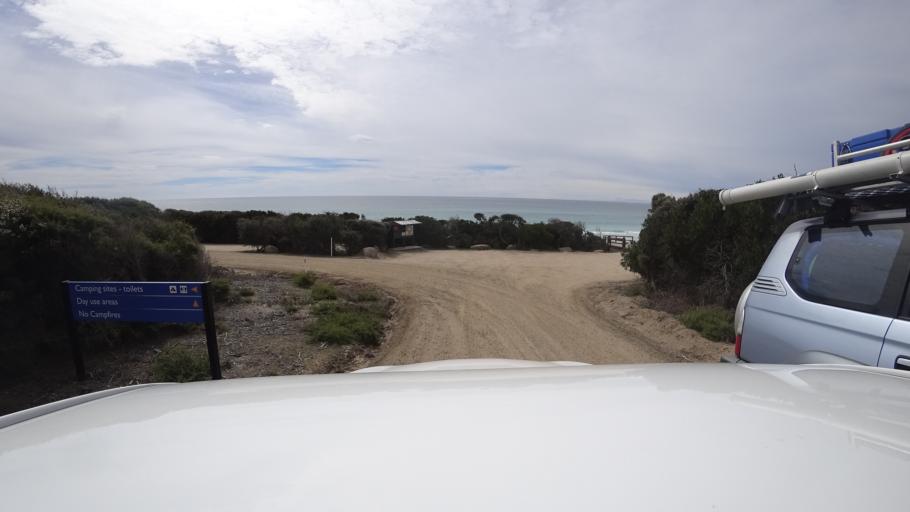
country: AU
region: Tasmania
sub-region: Break O'Day
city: St Helens
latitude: -41.9923
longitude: 148.2853
